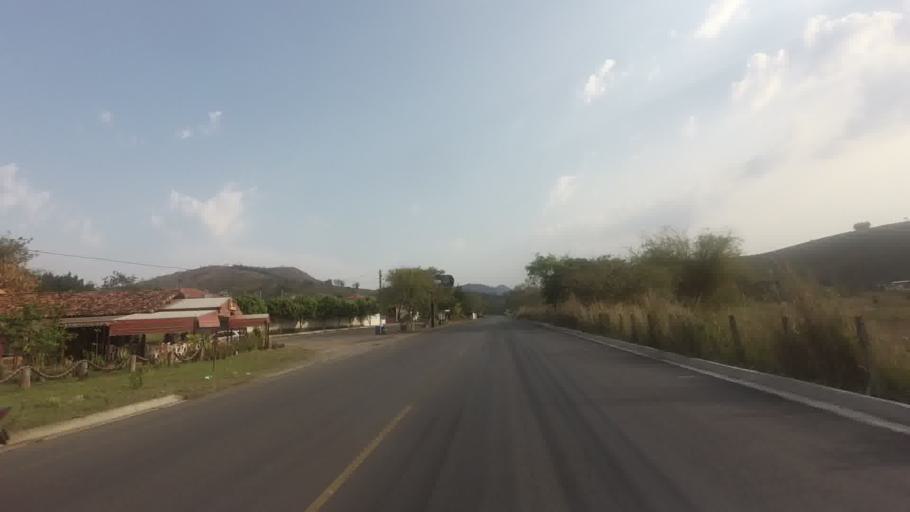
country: BR
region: Rio de Janeiro
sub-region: Cambuci
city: Cambuci
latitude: -21.4106
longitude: -41.9784
